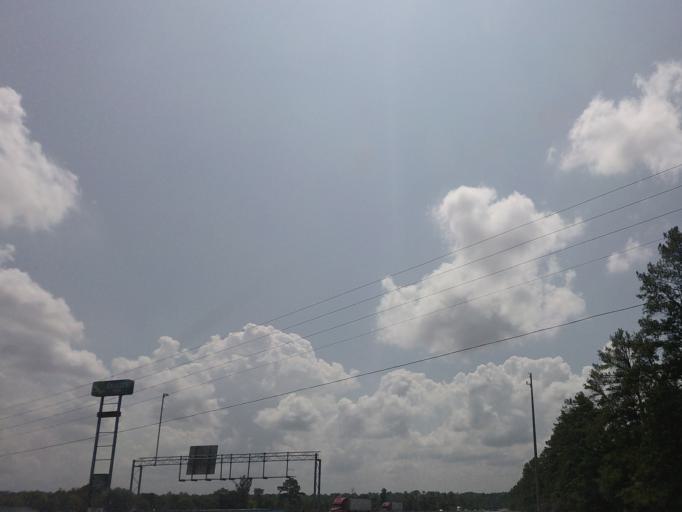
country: US
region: Georgia
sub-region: Bibb County
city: West Point
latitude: 32.8068
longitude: -83.7245
